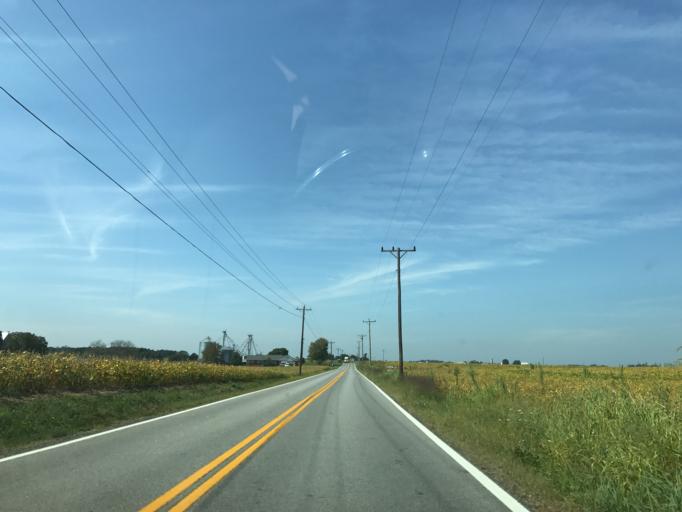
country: US
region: Maryland
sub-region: Queen Anne's County
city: Kingstown
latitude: 39.2743
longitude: -75.9464
